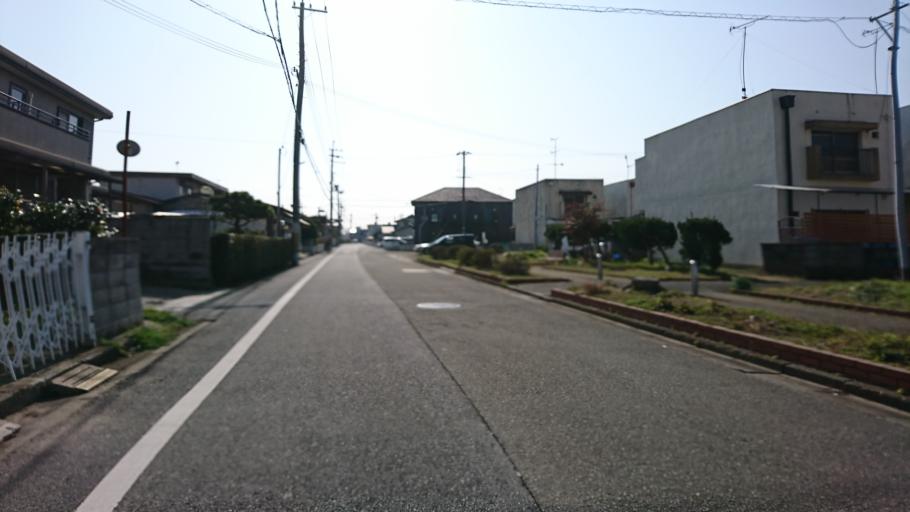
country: JP
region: Hyogo
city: Kakogawacho-honmachi
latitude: 34.7569
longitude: 134.8202
